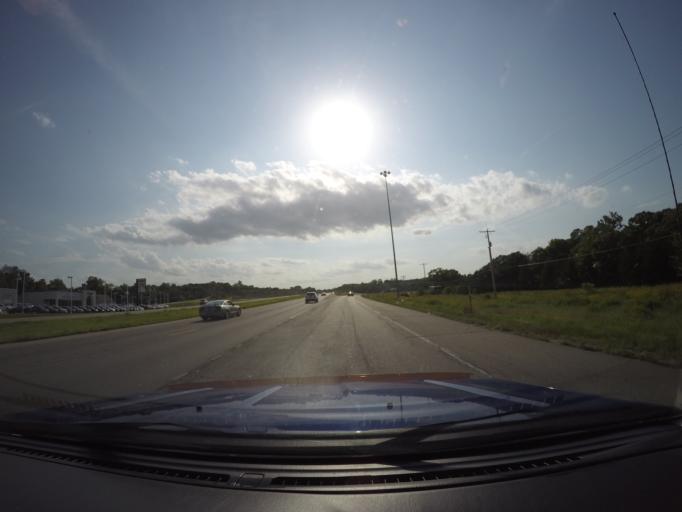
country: US
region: Kansas
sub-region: Riley County
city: Manhattan
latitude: 39.1690
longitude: -96.5997
